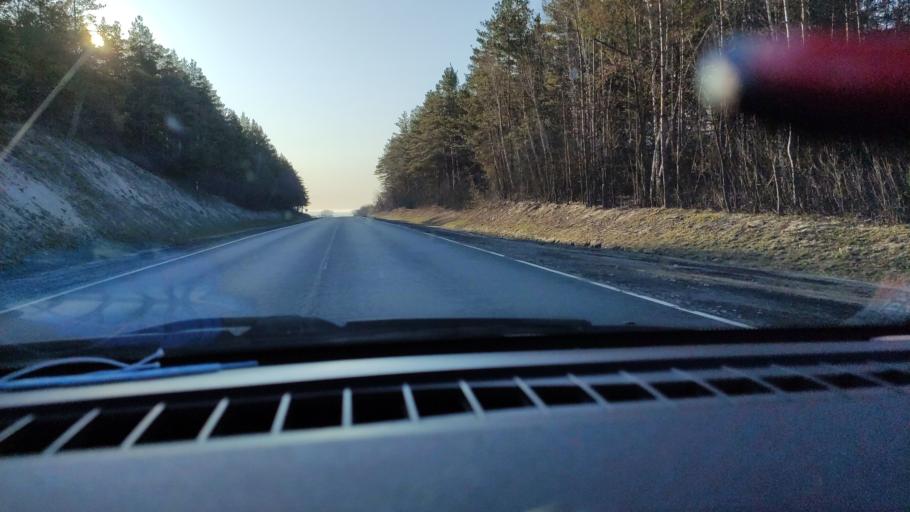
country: RU
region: Saratov
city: Vol'sk
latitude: 52.1046
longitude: 47.4410
